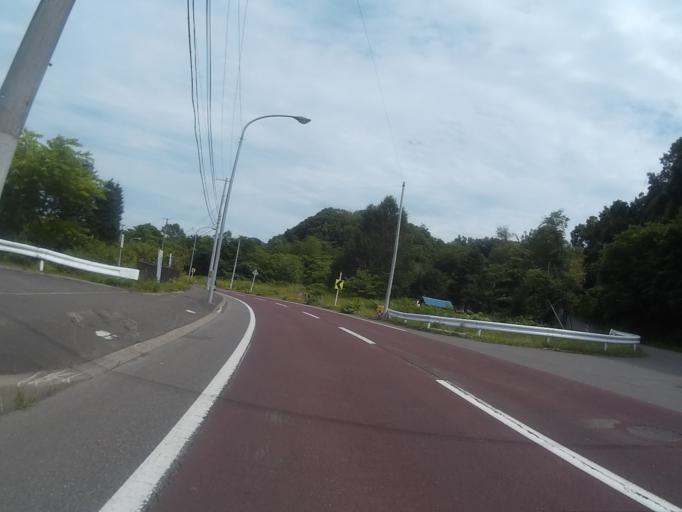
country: JP
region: Hokkaido
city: Sapporo
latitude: 42.9615
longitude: 141.2270
